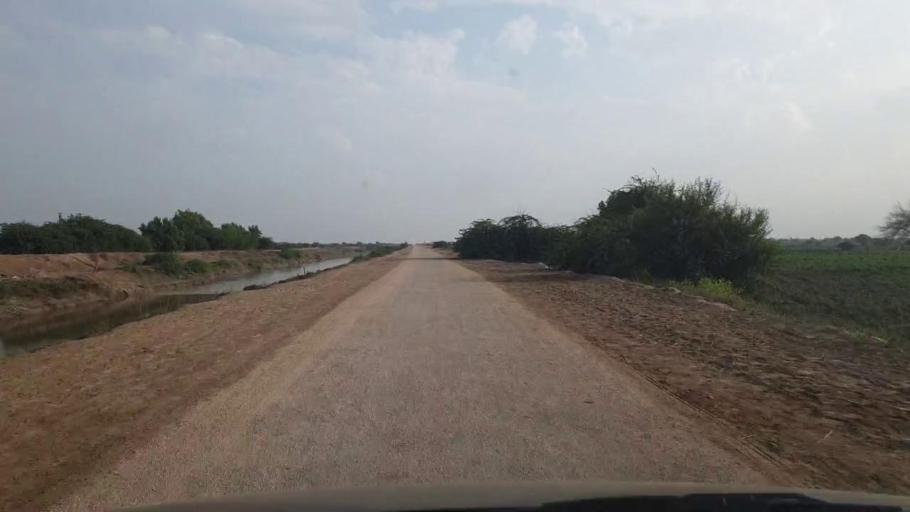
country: PK
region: Sindh
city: Badin
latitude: 24.5470
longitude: 68.6717
